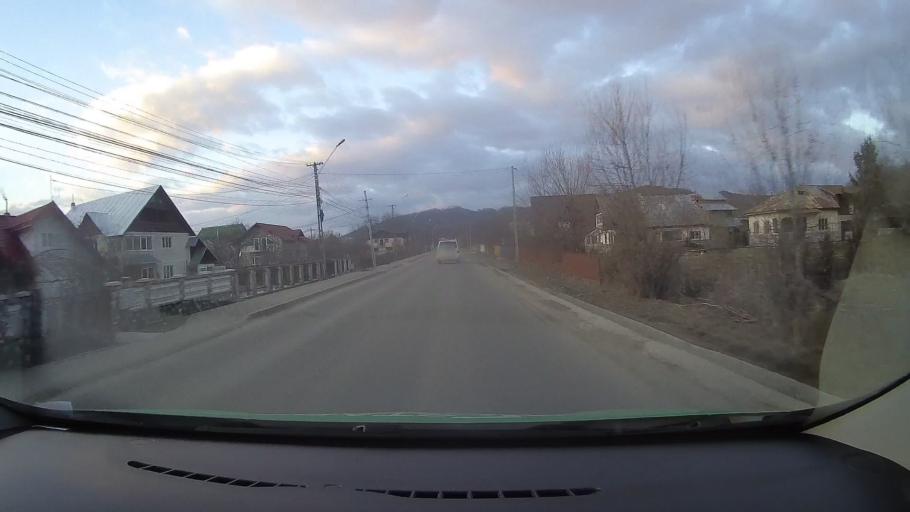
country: RO
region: Dambovita
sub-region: Municipiul Moreni
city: Moreni
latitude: 45.0022
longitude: 25.6468
